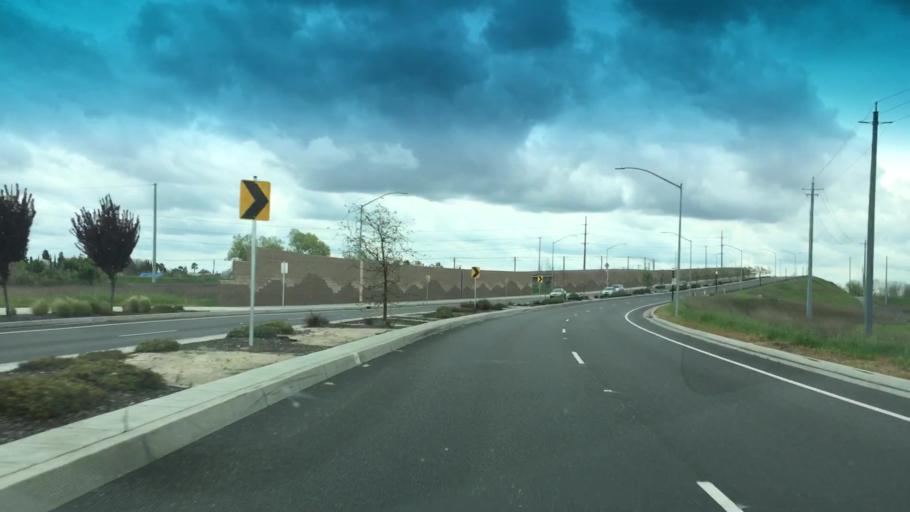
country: US
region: California
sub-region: Sacramento County
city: Parkway
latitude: 38.4624
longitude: -121.4668
